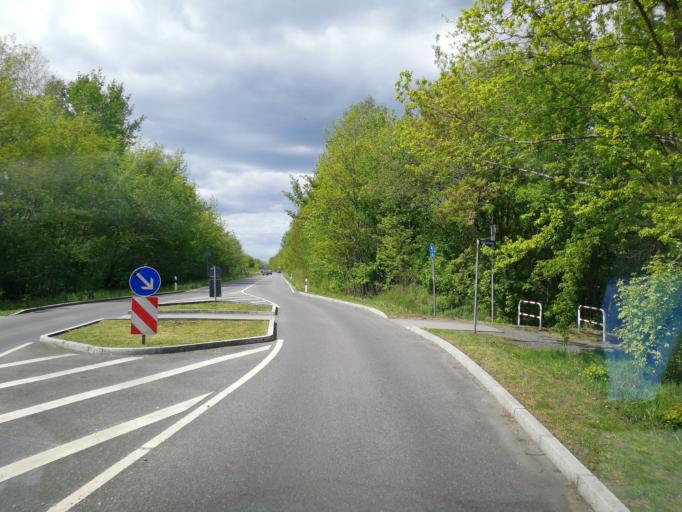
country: DE
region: Brandenburg
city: Lauchhammer
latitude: 51.4852
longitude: 13.7540
